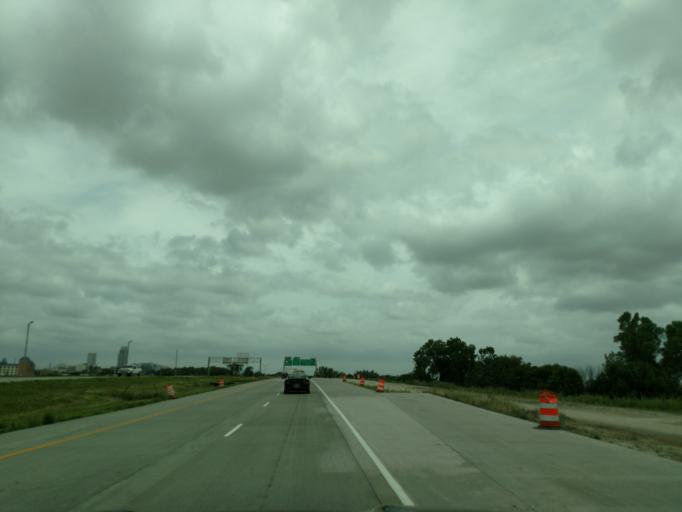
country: US
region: Nebraska
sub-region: Douglas County
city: Omaha
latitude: 41.2400
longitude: -95.9024
